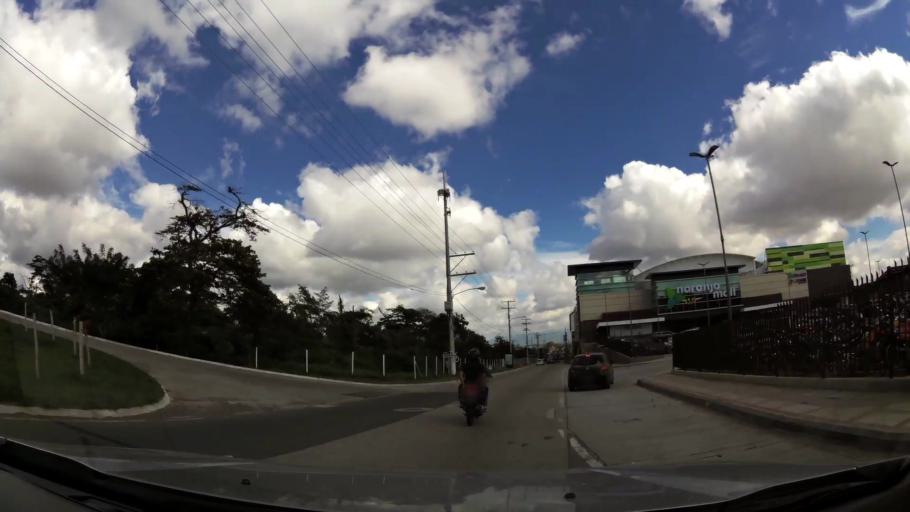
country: GT
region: Guatemala
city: Guatemala City
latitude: 14.6516
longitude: -90.5440
